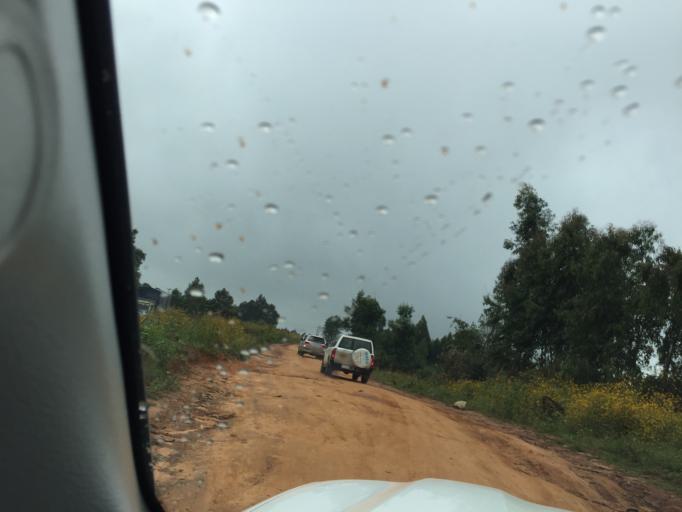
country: TZ
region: Iringa
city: Iringa
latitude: -7.9593
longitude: 35.8196
